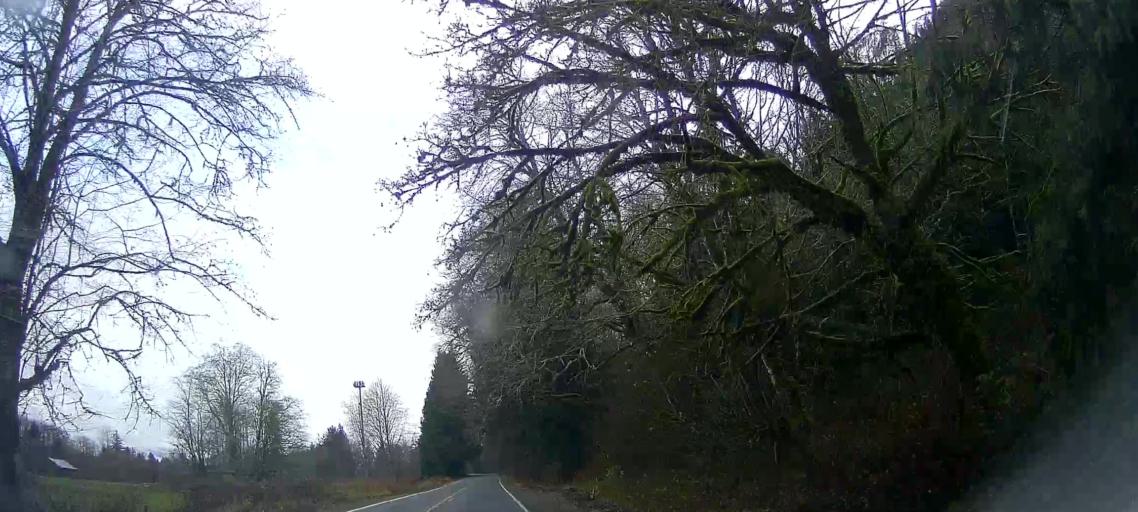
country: US
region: Washington
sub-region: Skagit County
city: Sedro-Woolley
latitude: 48.5141
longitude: -121.9437
